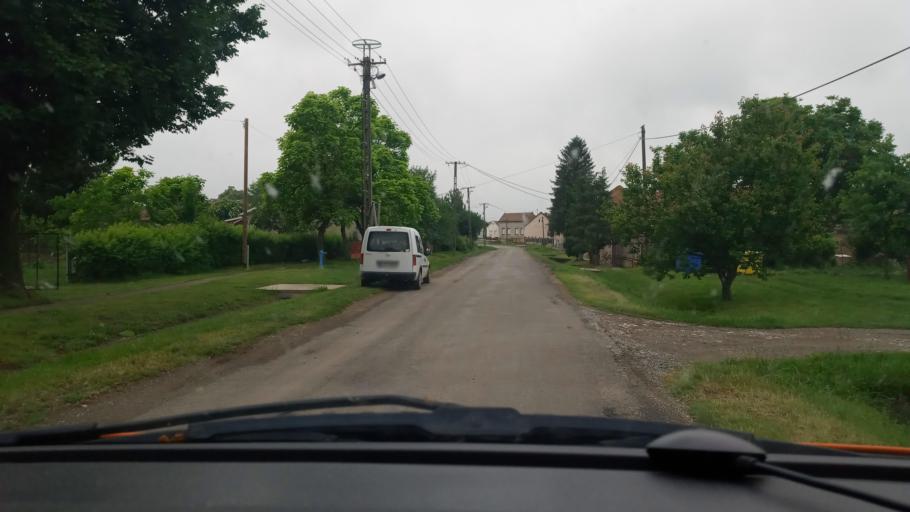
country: HU
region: Baranya
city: Szentlorinc
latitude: 46.0512
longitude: 17.9677
